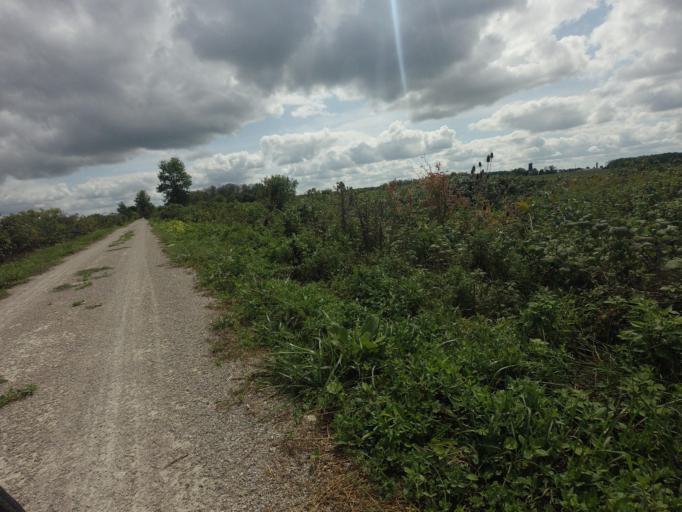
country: CA
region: Ontario
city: North Perth
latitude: 43.5705
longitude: -81.0343
